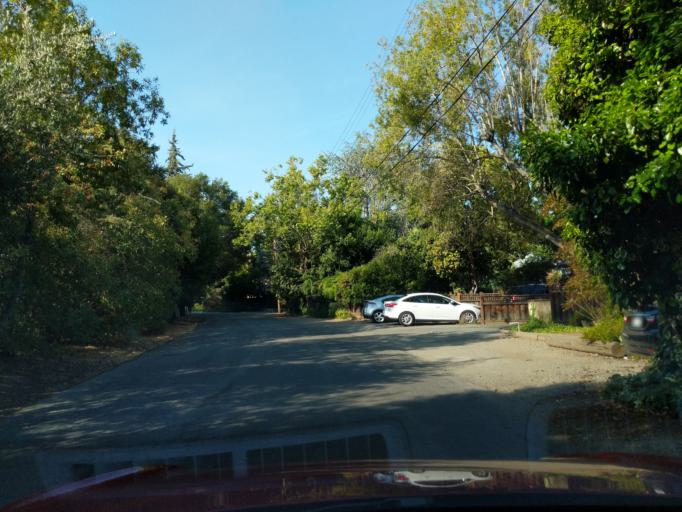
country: US
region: California
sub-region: San Mateo County
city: Menlo Park
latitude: 37.4445
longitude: -122.1748
